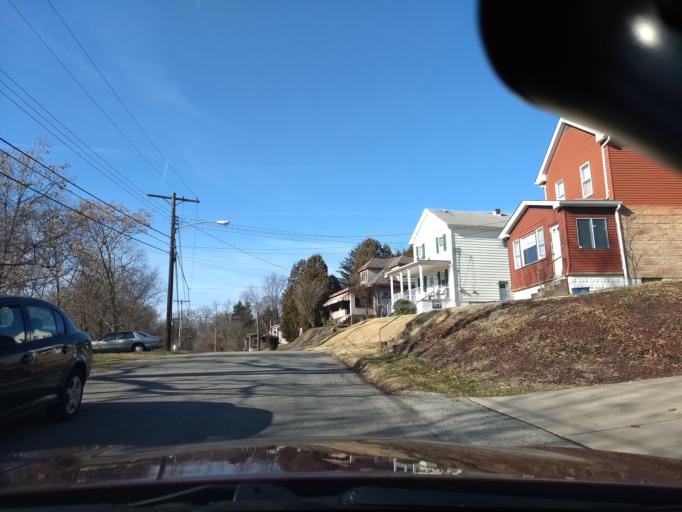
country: US
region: Pennsylvania
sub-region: Allegheny County
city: Whitaker
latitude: 40.3944
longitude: -79.8880
